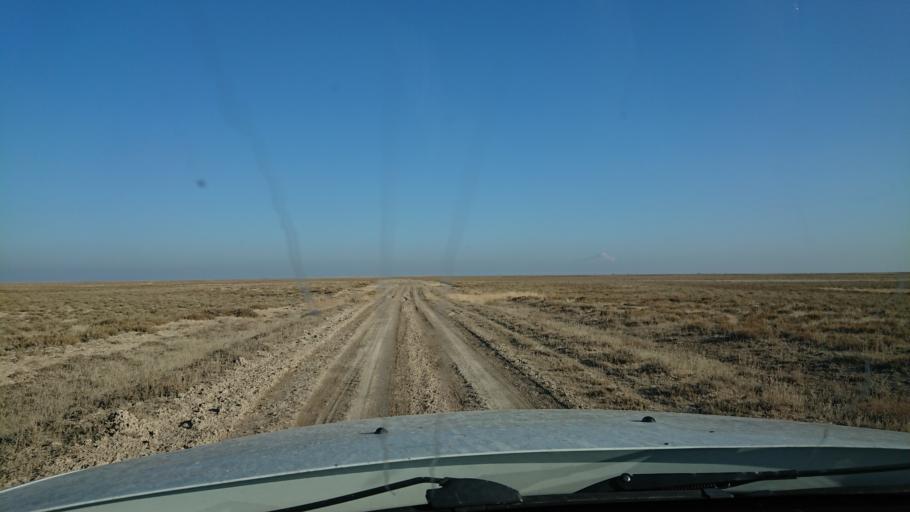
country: TR
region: Aksaray
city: Eskil
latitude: 38.4080
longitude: 33.5645
